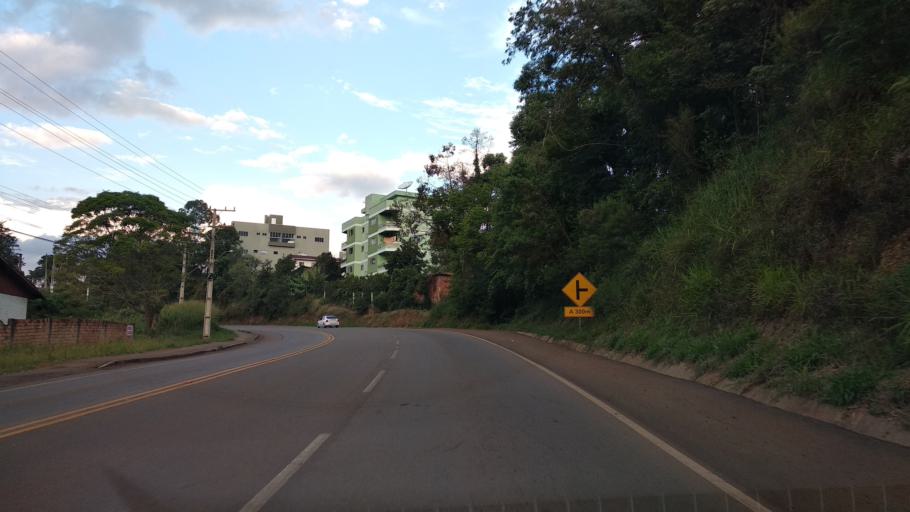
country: BR
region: Santa Catarina
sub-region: Videira
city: Videira
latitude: -27.0015
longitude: -51.1241
